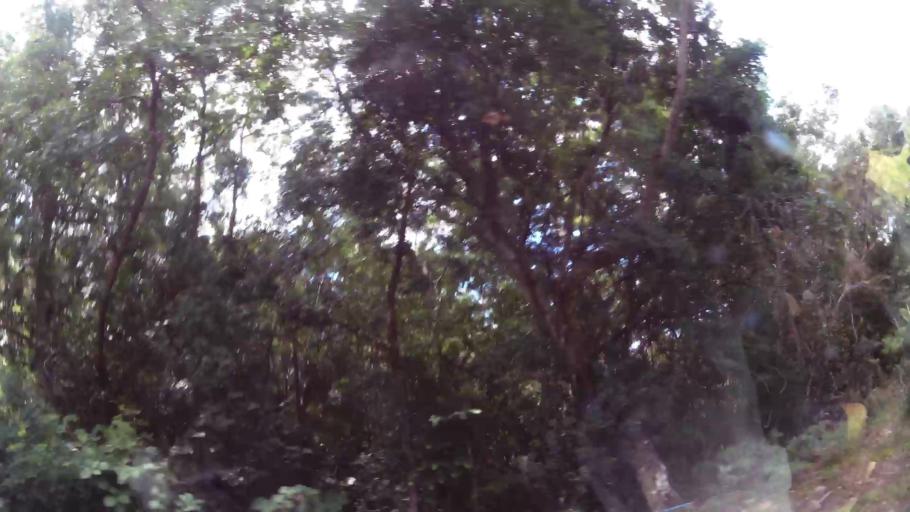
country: DM
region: Saint John
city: Portsmouth
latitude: 15.6357
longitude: -61.4573
